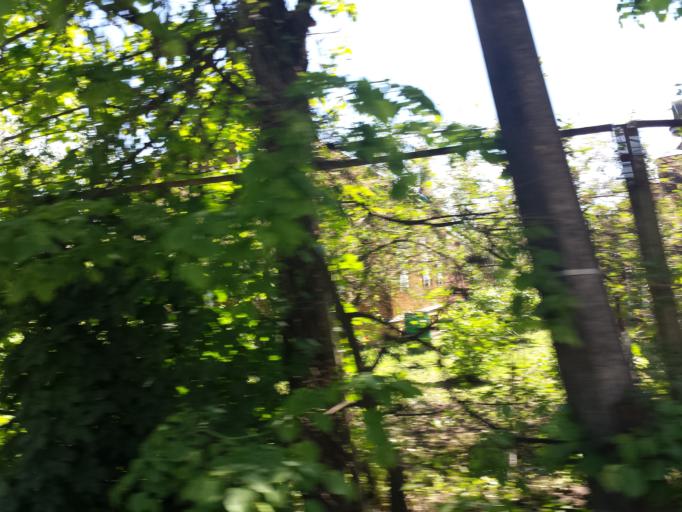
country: RU
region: Moscow
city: Lianozovo
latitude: 55.9280
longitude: 37.6150
